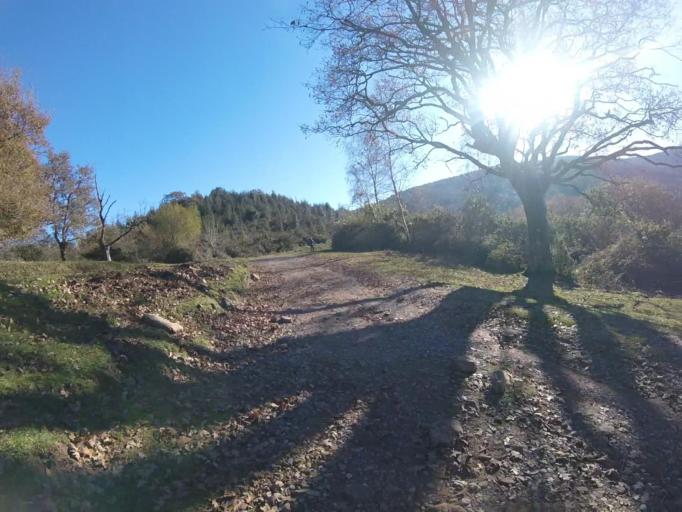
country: ES
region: Navarre
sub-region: Provincia de Navarra
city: Bera
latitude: 43.3207
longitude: -1.6996
